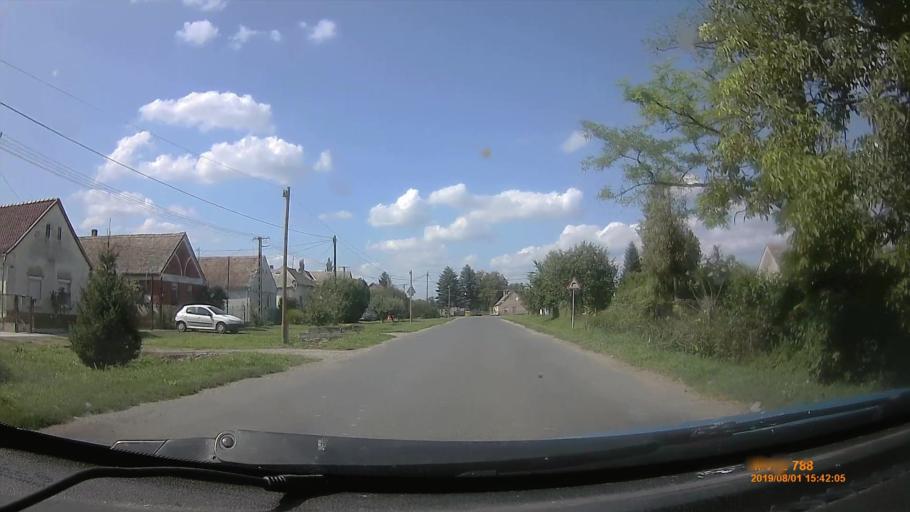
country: HU
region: Baranya
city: Szentlorinc
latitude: 45.9951
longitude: 17.9619
